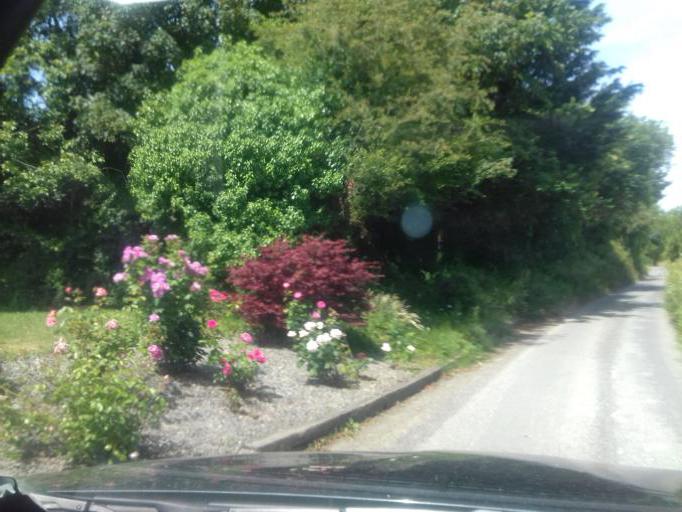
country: IE
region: Leinster
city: Lusk
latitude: 53.5336
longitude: -6.1554
